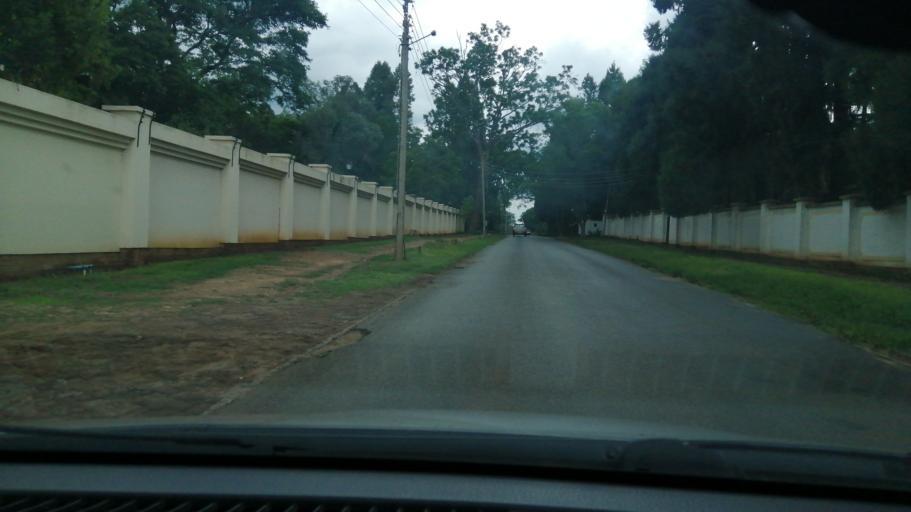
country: ZW
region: Harare
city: Harare
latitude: -17.7729
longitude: 31.0951
